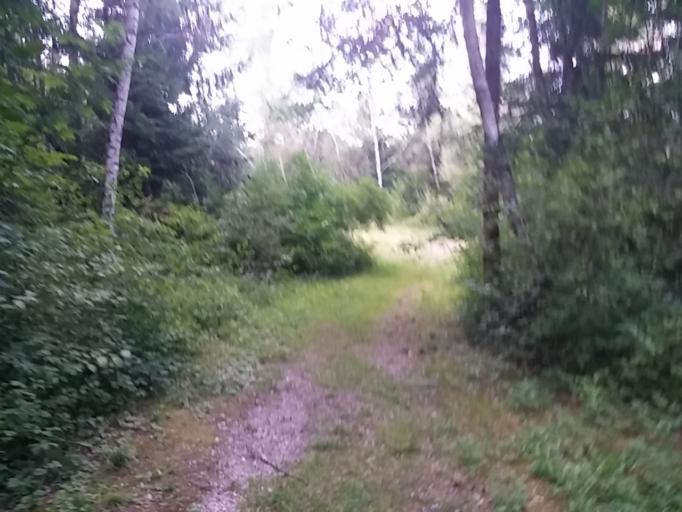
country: DE
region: Baden-Wuerttemberg
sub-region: Tuebingen Region
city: Aitrach
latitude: 47.9348
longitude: 10.0869
